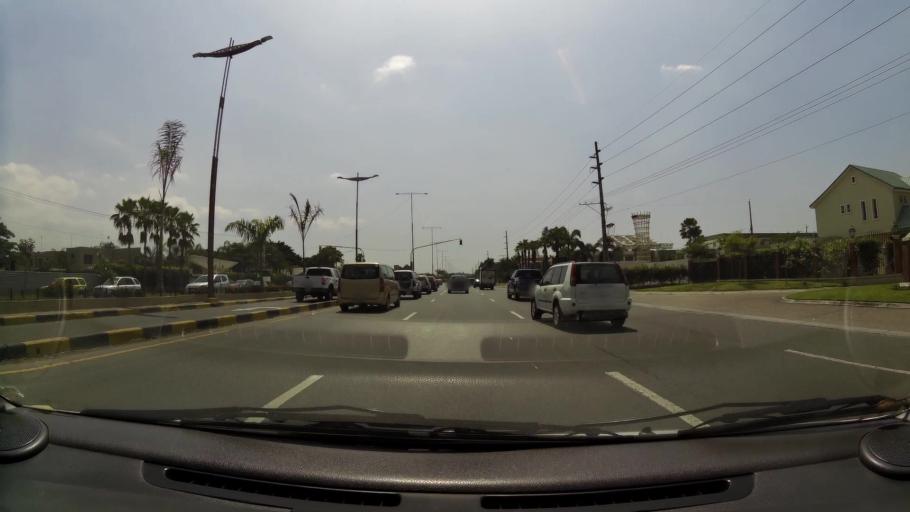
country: EC
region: Guayas
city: Eloy Alfaro
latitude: -2.1073
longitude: -79.8722
